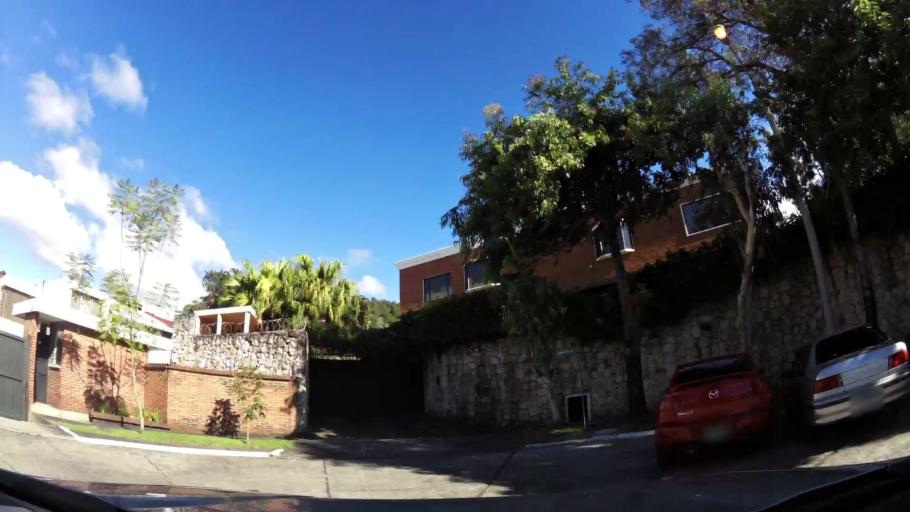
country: GT
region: Guatemala
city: Santa Catarina Pinula
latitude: 14.5682
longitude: -90.5256
